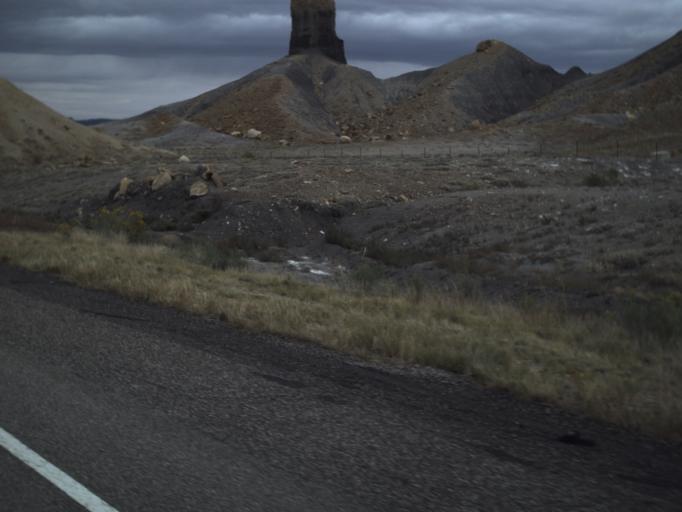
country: US
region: Utah
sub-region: Emery County
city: Ferron
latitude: 38.8104
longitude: -111.2170
